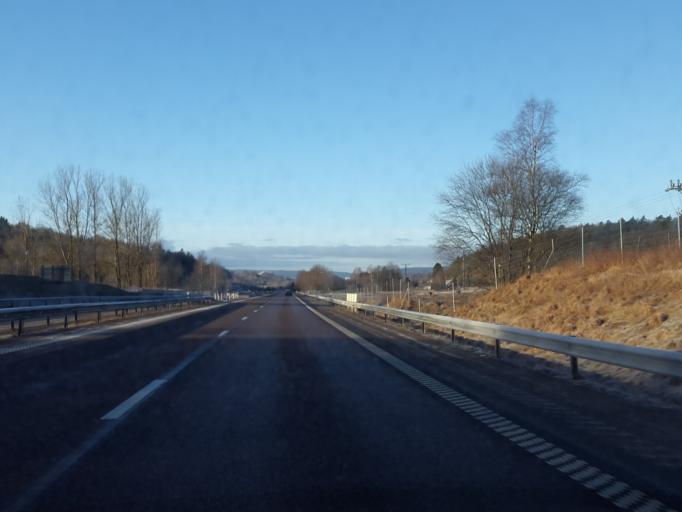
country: SE
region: Vaestra Goetaland
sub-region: Lerums Kommun
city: Stenkullen
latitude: 57.7888
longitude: 12.3314
